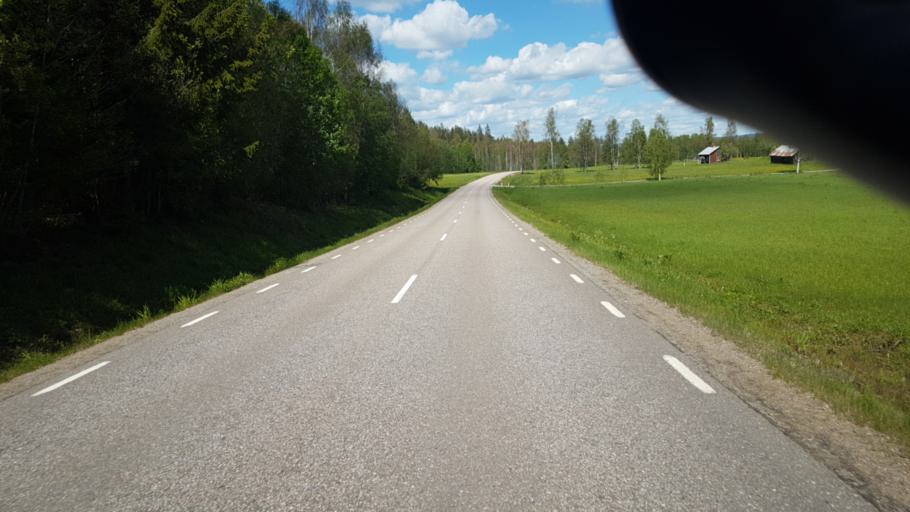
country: SE
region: Vaermland
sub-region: Arvika Kommun
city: Arvika
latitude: 59.6342
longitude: 12.8866
